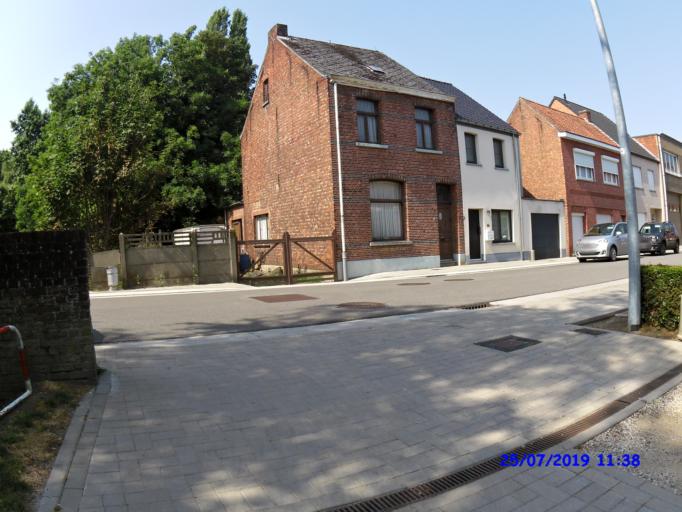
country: BE
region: Flanders
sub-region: Provincie Antwerpen
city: Mol
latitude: 51.1893
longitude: 5.1255
